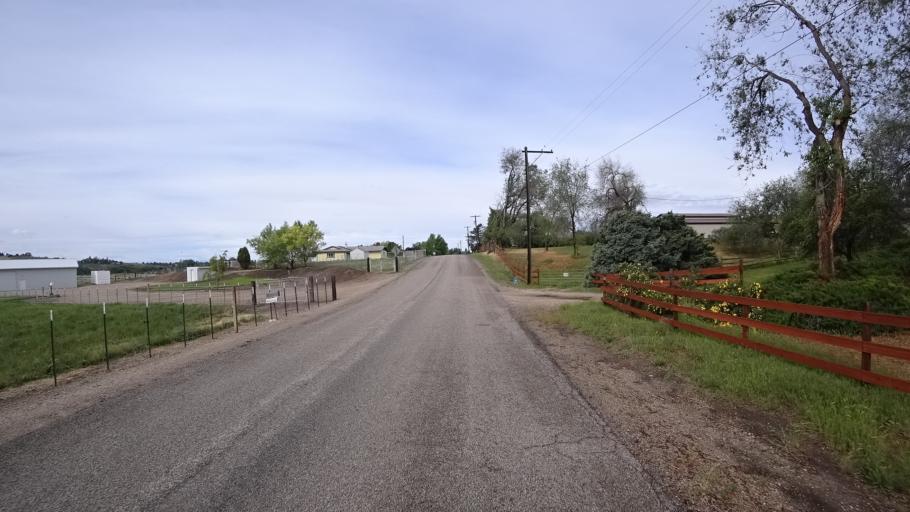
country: US
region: Idaho
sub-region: Ada County
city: Eagle
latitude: 43.7323
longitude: -116.3147
